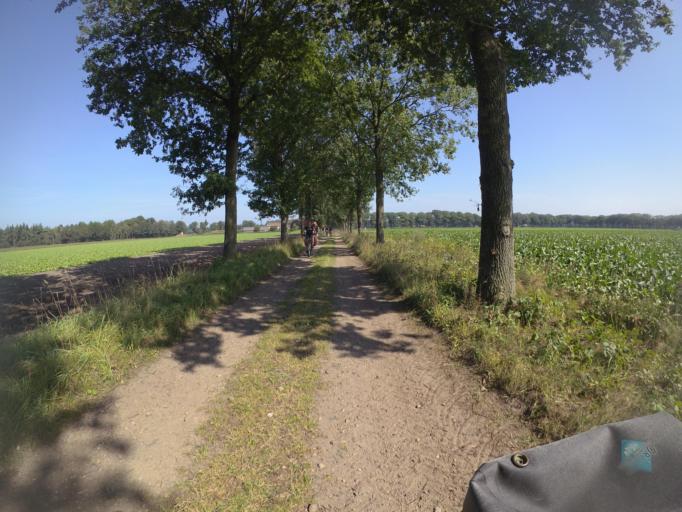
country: NL
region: North Brabant
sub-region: Gemeente Mill en Sint Hubert
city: Wilbertoord
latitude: 51.5690
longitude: 5.8023
